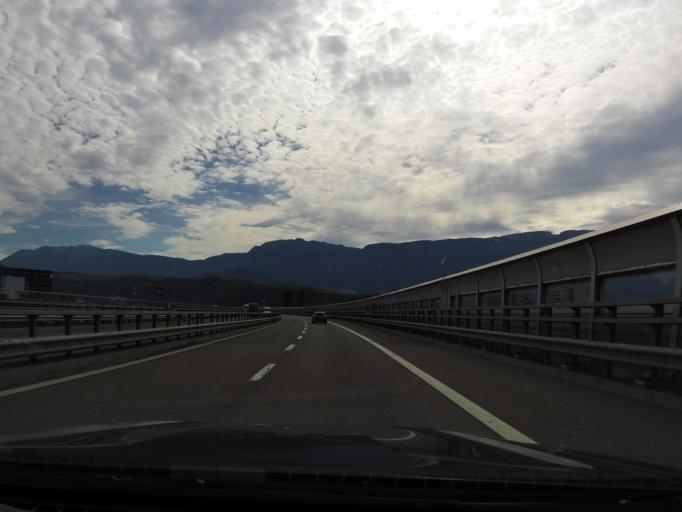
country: IT
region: Trentino-Alto Adige
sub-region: Bolzano
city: Bolzano
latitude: 46.4850
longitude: 11.3309
